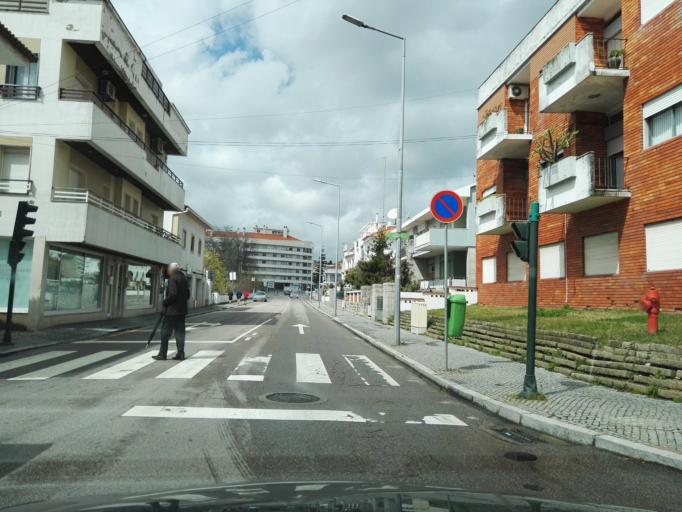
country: PT
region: Portalegre
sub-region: Portalegre
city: Portalegre
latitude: 39.2992
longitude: -7.4297
